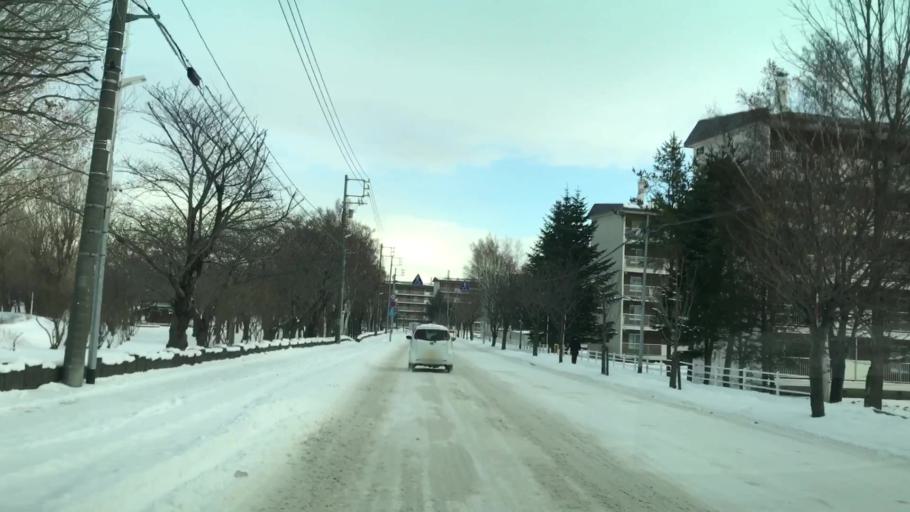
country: JP
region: Hokkaido
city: Sapporo
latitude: 43.0851
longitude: 141.3031
